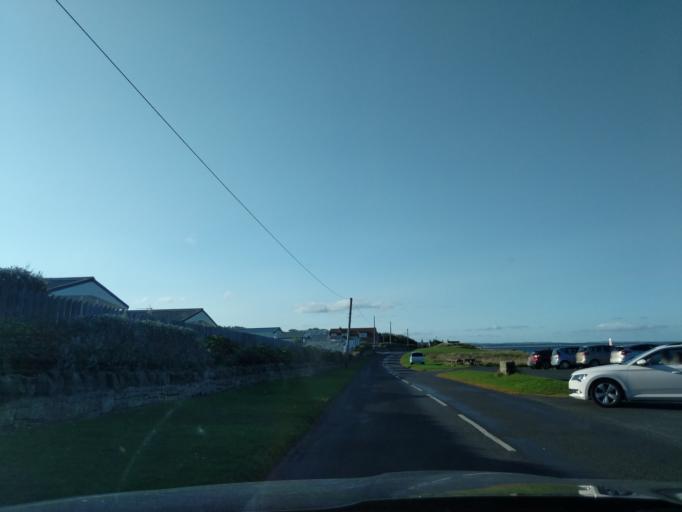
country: GB
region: England
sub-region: Northumberland
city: Lynemouth
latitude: 55.2301
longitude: -1.5315
